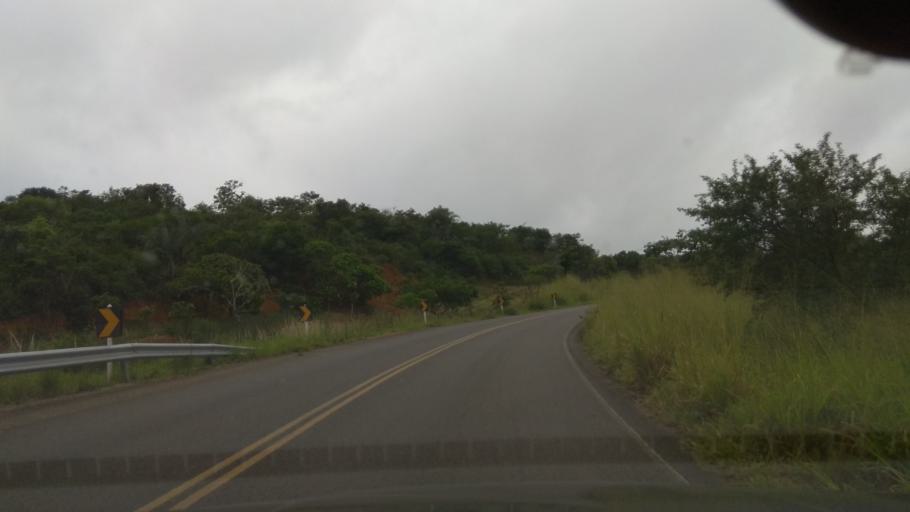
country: BR
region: Bahia
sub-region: Santa Ines
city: Santa Ines
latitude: -13.2383
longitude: -39.7503
